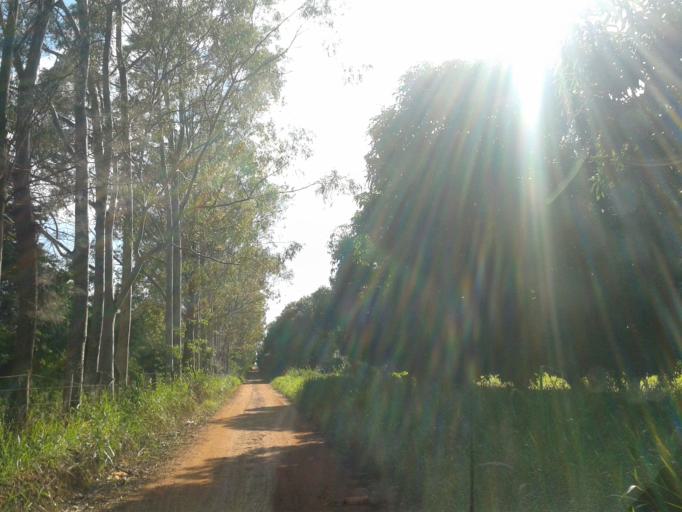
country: BR
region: Minas Gerais
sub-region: Centralina
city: Centralina
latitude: -18.7218
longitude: -49.1612
